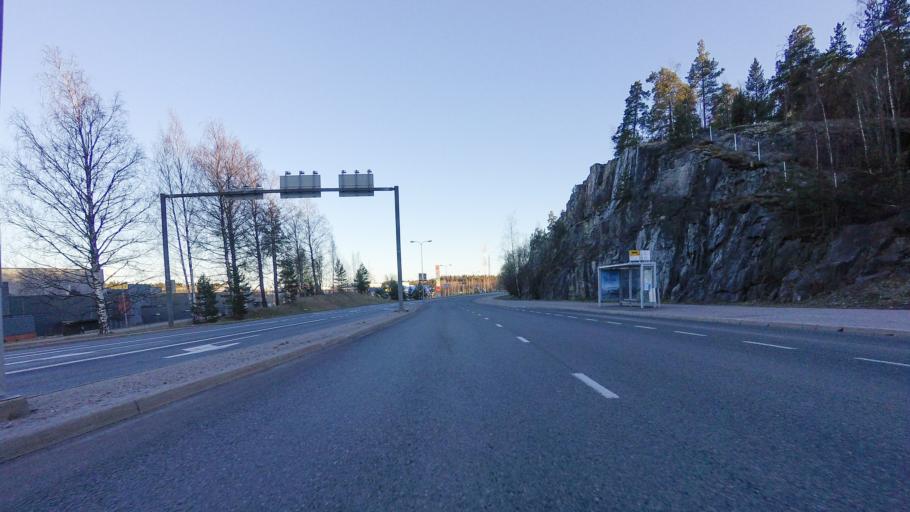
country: FI
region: Uusimaa
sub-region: Helsinki
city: Vantaa
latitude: 60.2818
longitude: 25.0794
